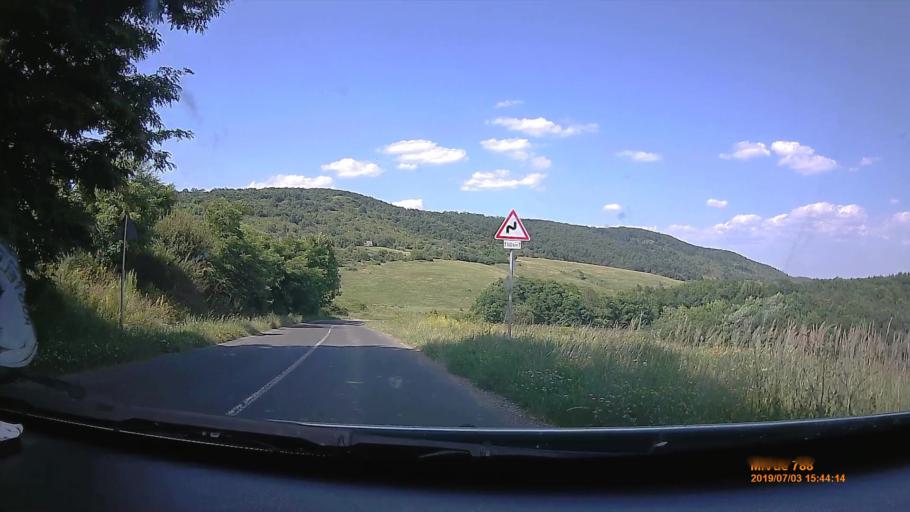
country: HU
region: Heves
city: Szilvasvarad
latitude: 48.1740
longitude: 20.4447
